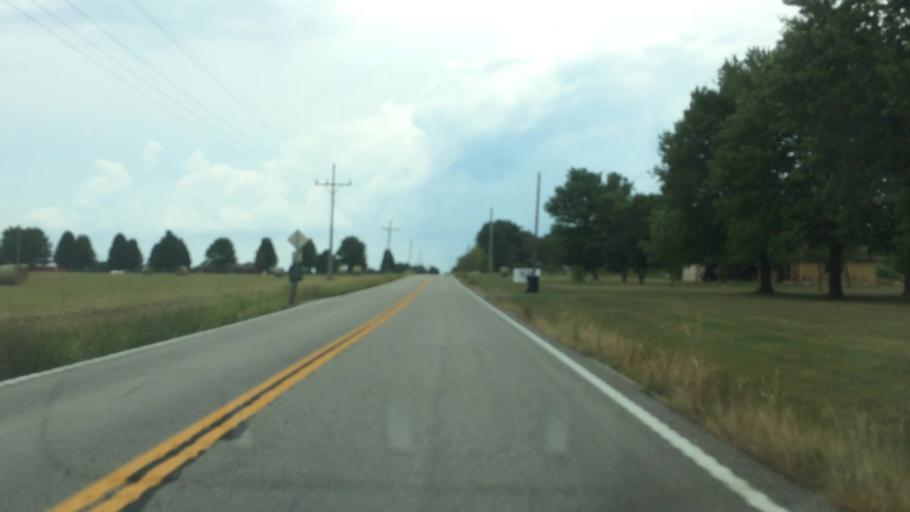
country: US
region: Missouri
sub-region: Greene County
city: Strafford
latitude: 37.2450
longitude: -93.1354
